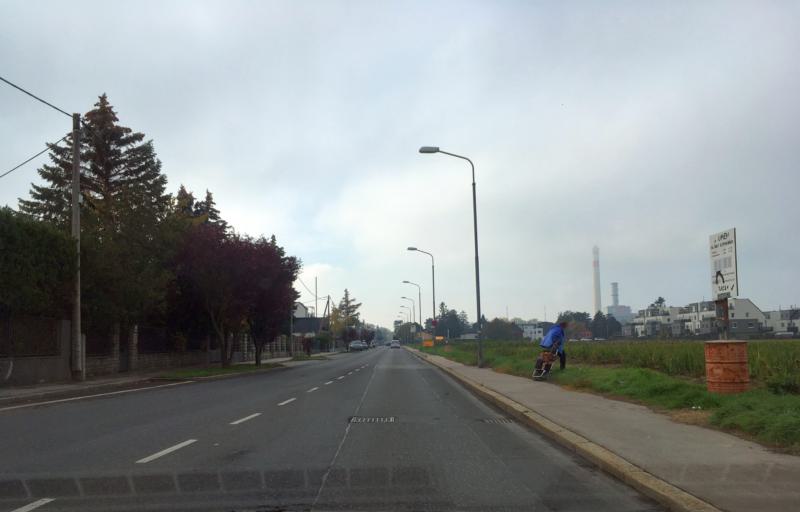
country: AT
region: Lower Austria
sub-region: Politischer Bezirk Wien-Umgebung
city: Schwechat
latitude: 48.2040
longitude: 16.4756
